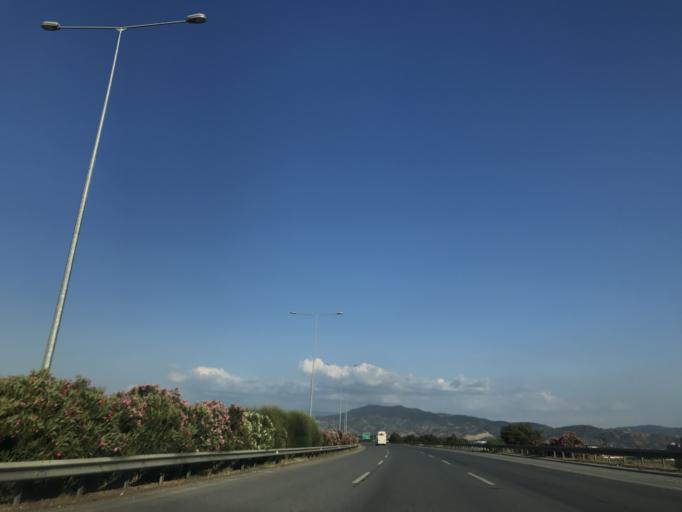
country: TR
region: Aydin
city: Aydin
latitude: 37.8246
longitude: 27.8150
